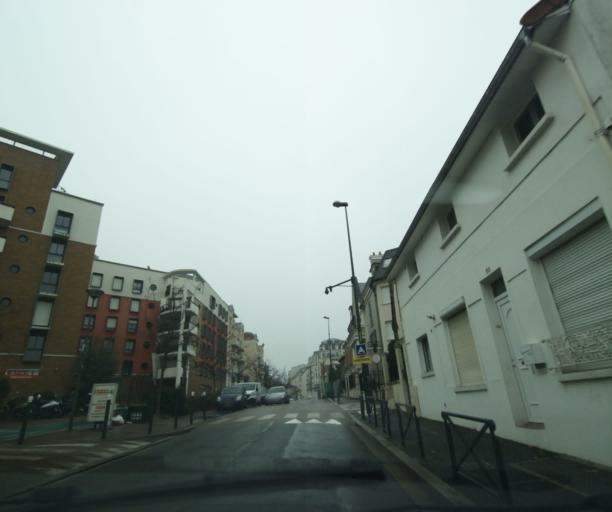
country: FR
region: Ile-de-France
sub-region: Departement des Hauts-de-Seine
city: Suresnes
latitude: 48.8817
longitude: 2.2257
